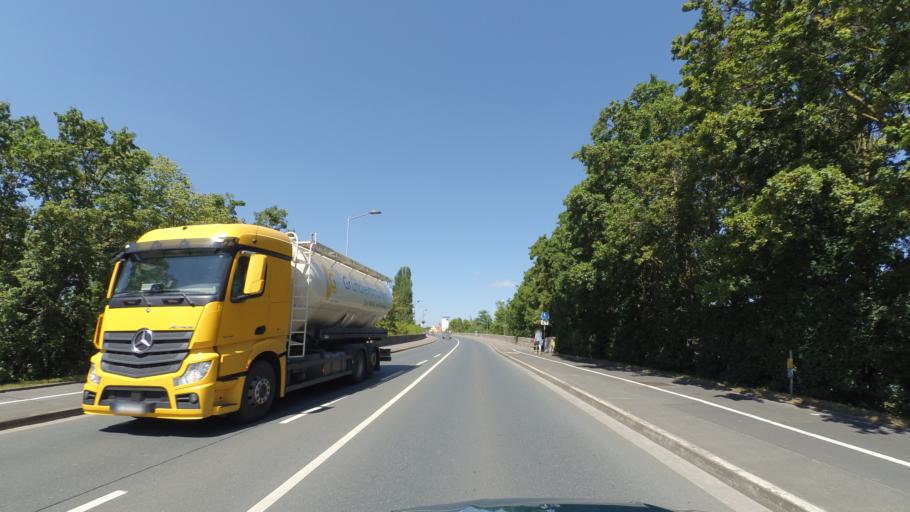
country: DE
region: Bavaria
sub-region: Regierungsbezirk Unterfranken
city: Kitzingen
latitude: 49.7350
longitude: 10.1702
